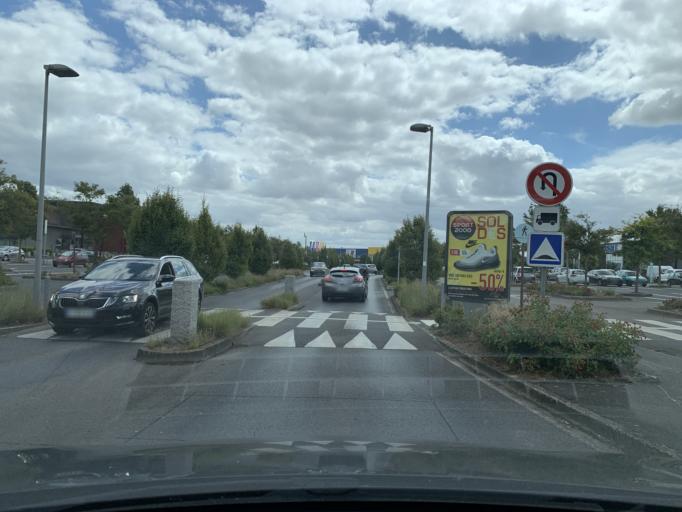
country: FR
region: Nord-Pas-de-Calais
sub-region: Departement du Pas-de-Calais
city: Henin-Beaumont
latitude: 50.3951
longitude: 2.9737
